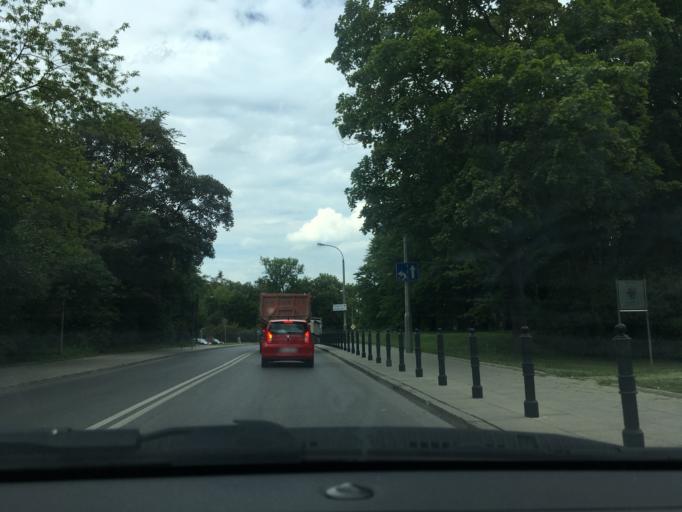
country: PL
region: Masovian Voivodeship
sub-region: Warszawa
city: Zoliborz
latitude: 52.2565
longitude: 21.0049
